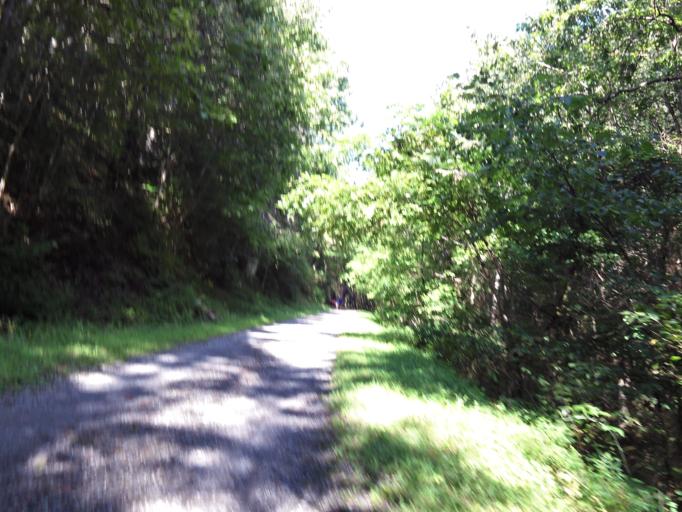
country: US
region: Virginia
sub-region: Washington County
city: Abingdon
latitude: 36.6869
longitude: -81.9412
